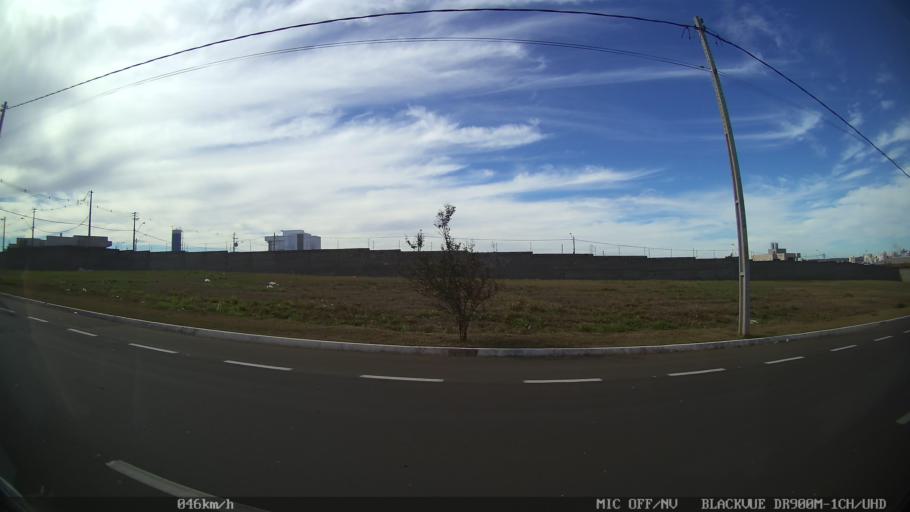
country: BR
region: Sao Paulo
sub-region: Catanduva
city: Catanduva
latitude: -21.1168
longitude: -48.9778
